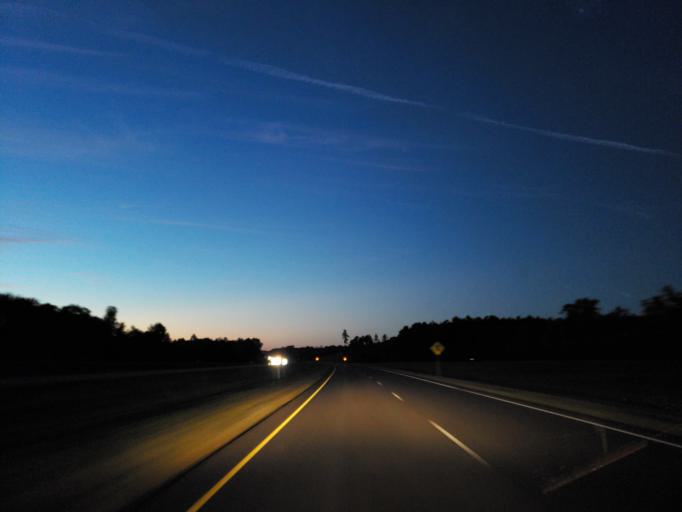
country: US
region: Mississippi
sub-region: Clarke County
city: Quitman
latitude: 32.0615
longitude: -88.6791
